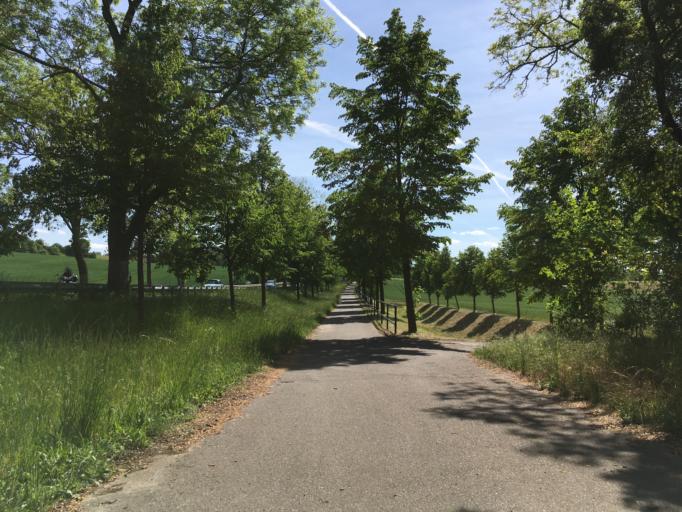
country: DE
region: Brandenburg
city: Oderberg
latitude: 52.8307
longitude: 14.0748
